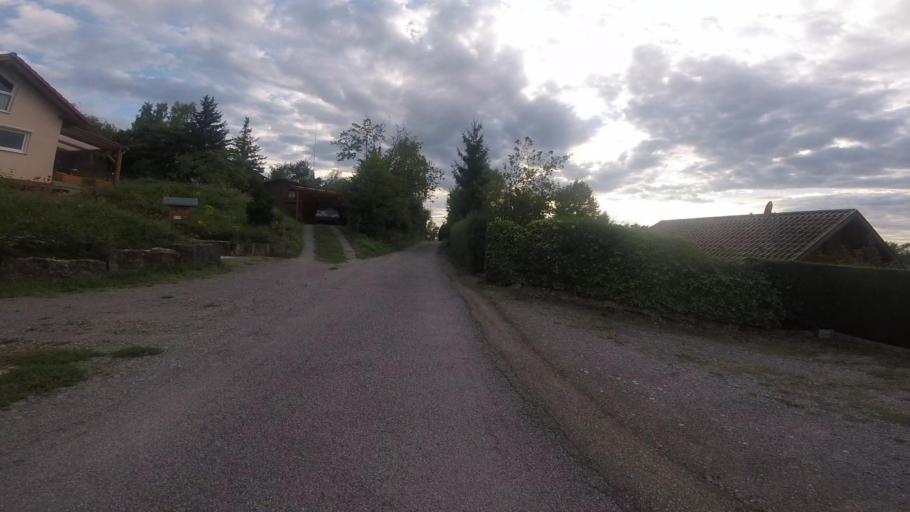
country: DE
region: Baden-Wuerttemberg
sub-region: Regierungsbezirk Stuttgart
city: Beilstein
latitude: 49.0516
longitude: 9.3148
